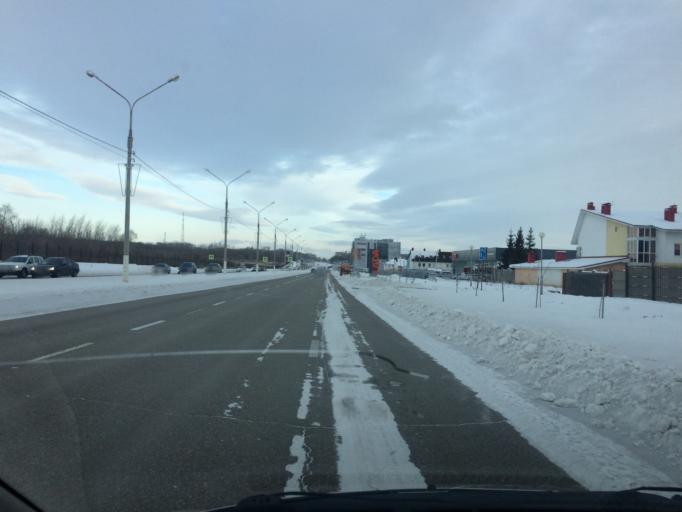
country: RU
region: Chelyabinsk
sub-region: Gorod Magnitogorsk
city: Magnitogorsk
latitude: 53.3824
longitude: 58.9618
